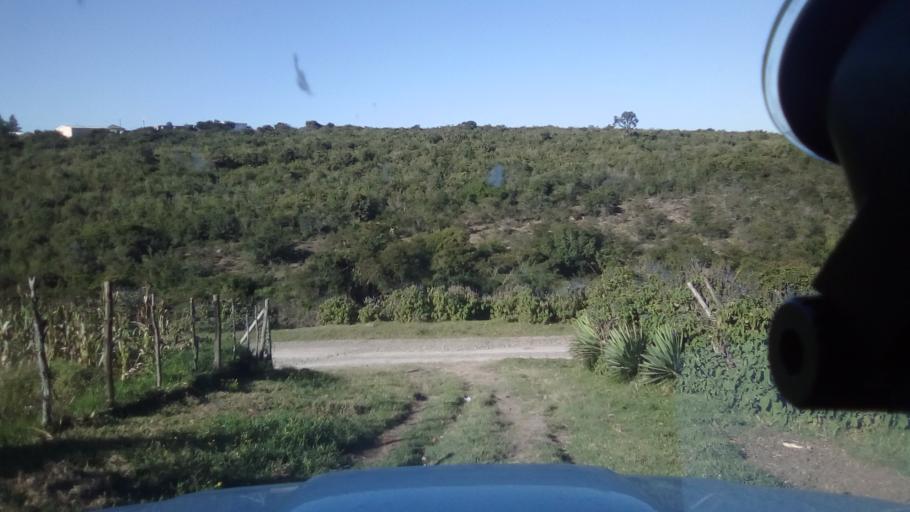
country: ZA
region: Eastern Cape
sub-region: Buffalo City Metropolitan Municipality
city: Bhisho
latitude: -32.8005
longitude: 27.3409
